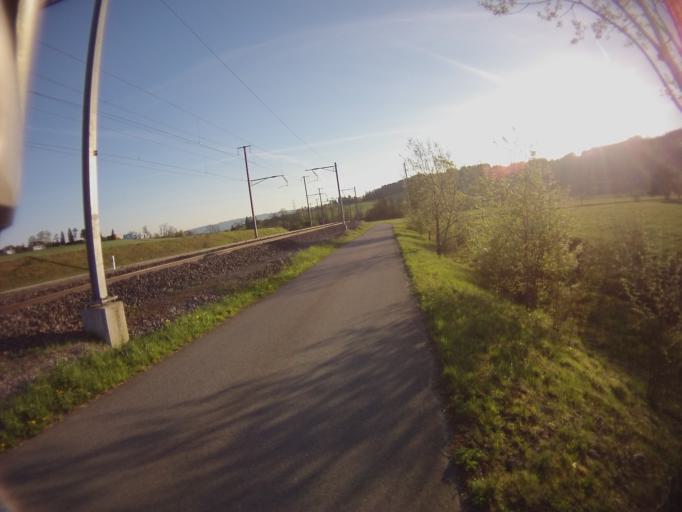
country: CH
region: Zurich
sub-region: Bezirk Affoltern
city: Hedingen
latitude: 47.3072
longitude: 8.4465
